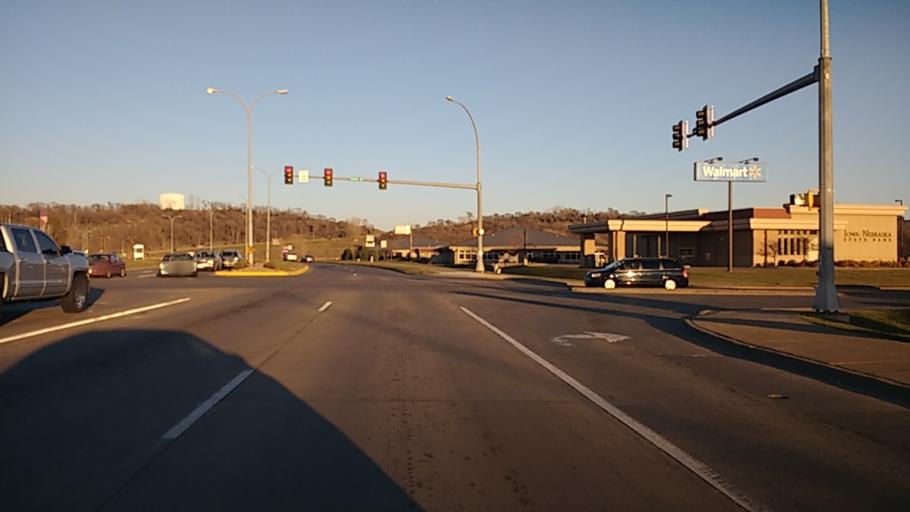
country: US
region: Iowa
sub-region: Woodbury County
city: Sergeant Bluff
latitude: 42.4361
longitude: -96.3647
